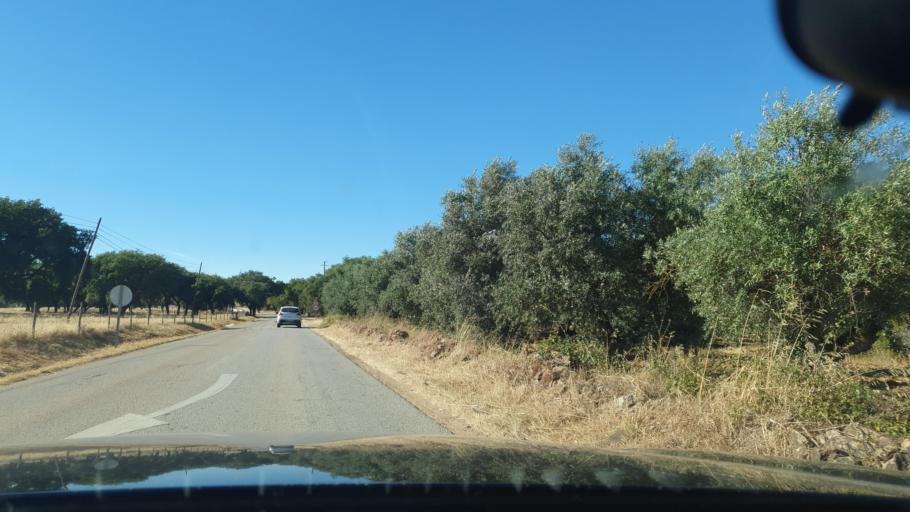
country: PT
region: Evora
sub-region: Alandroal
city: Alandroal
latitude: 38.7374
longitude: -7.4037
